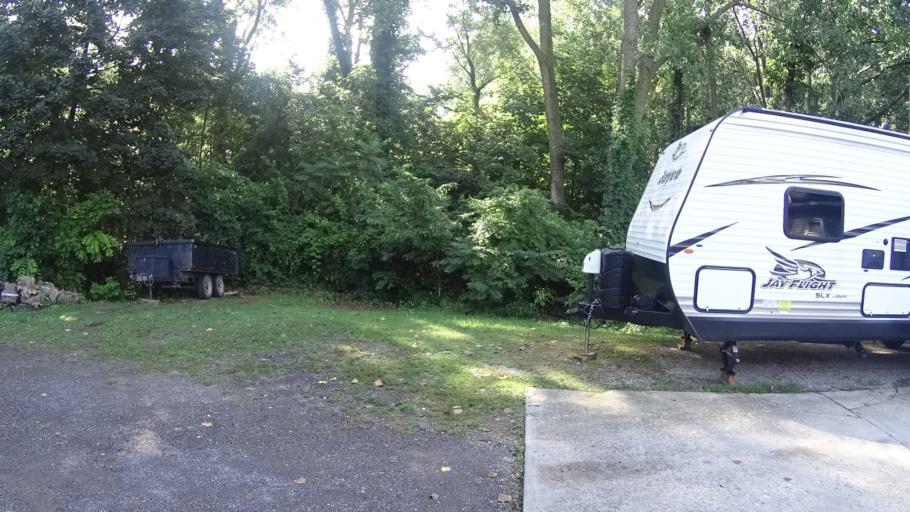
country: US
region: Ohio
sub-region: Erie County
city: Sandusky
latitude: 41.4352
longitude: -82.6843
